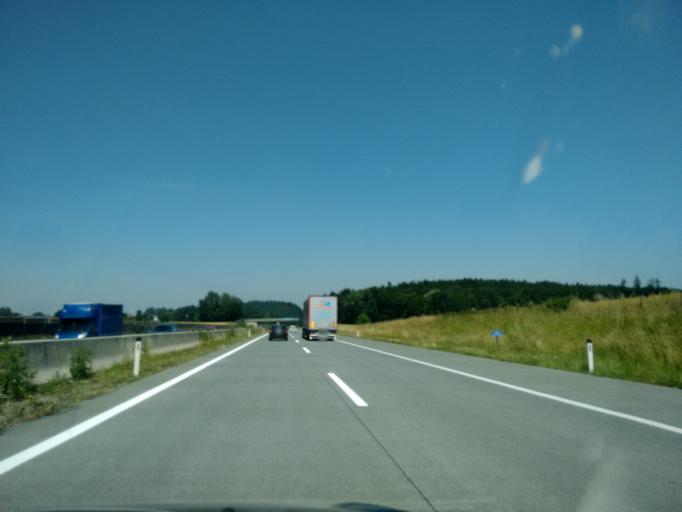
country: AT
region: Upper Austria
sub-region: Politischer Bezirk Vocklabruck
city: Desselbrunn
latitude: 47.9832
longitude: 13.7754
